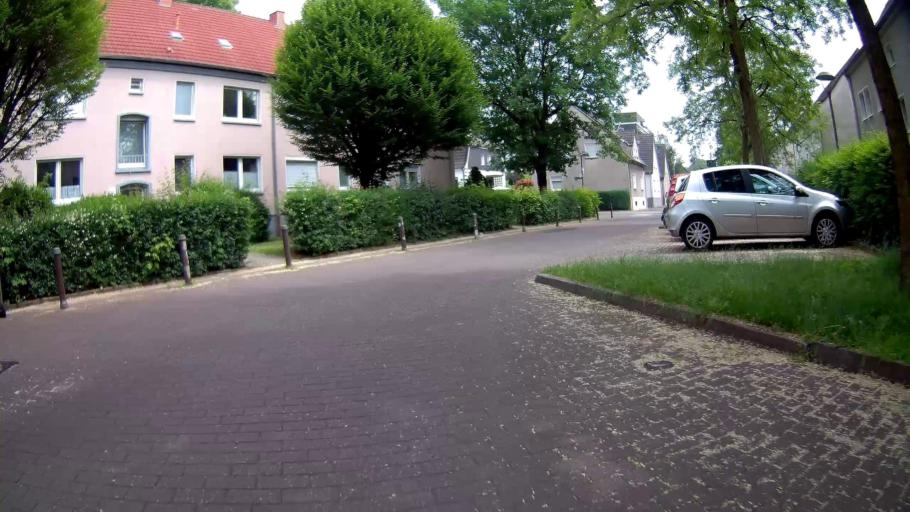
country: DE
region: North Rhine-Westphalia
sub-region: Regierungsbezirk Munster
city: Gladbeck
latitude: 51.5684
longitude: 7.0525
